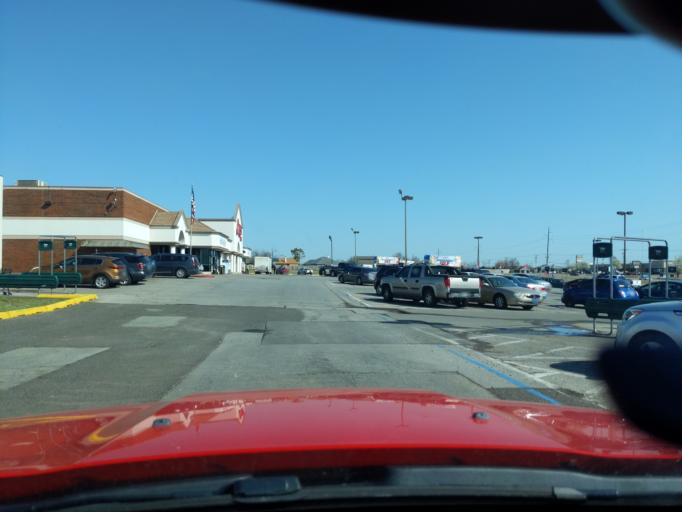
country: US
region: Oklahoma
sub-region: Cleveland County
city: Moore
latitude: 35.3490
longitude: -97.4782
